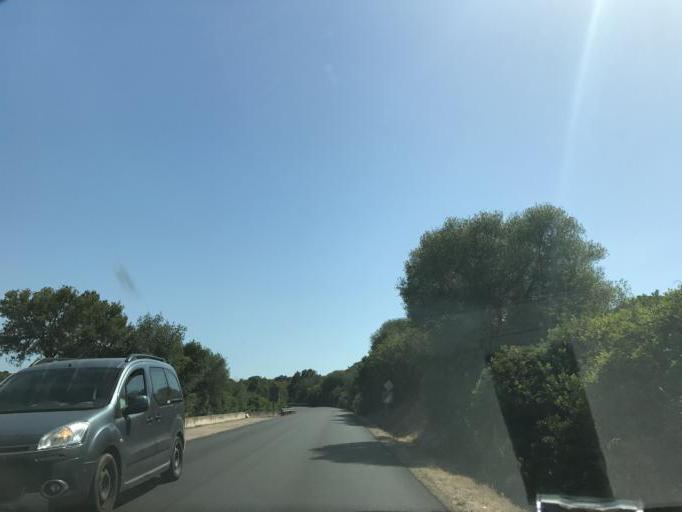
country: IT
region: Sardinia
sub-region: Provincia di Olbia-Tempio
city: San Teodoro
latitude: 40.8302
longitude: 9.6631
